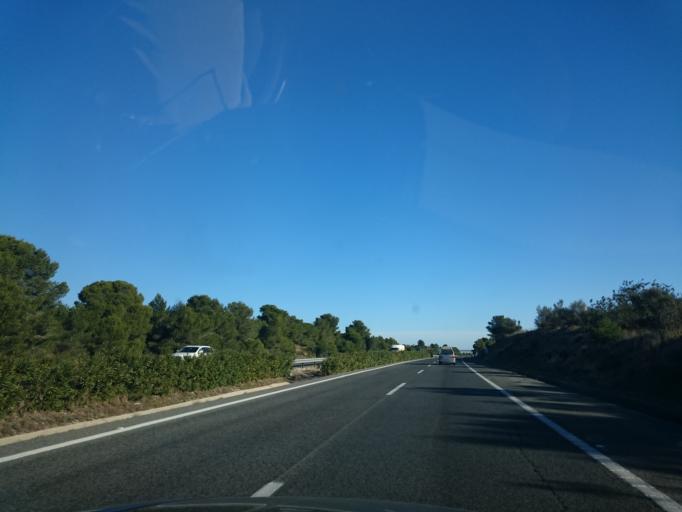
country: ES
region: Catalonia
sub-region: Provincia de Tarragona
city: L'Ampolla
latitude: 40.8256
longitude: 0.7288
